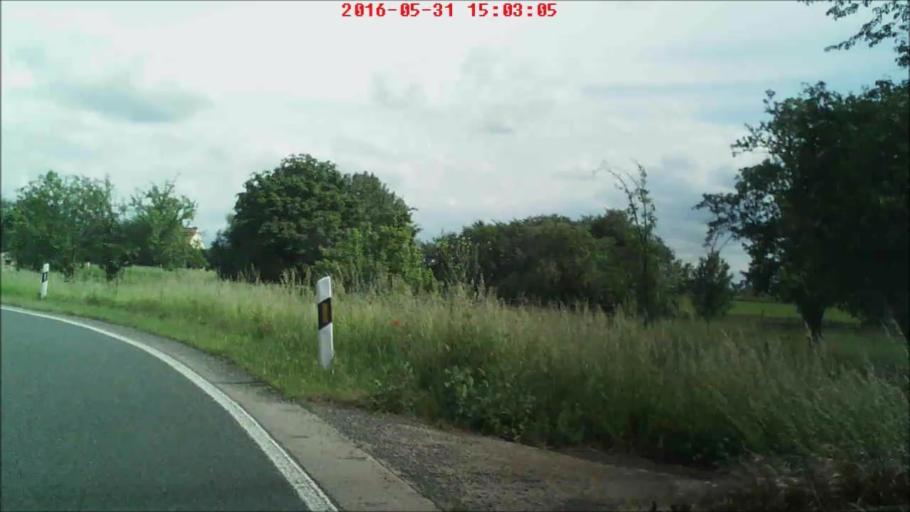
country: DE
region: Thuringia
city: Straussfurt
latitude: 51.1497
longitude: 10.9855
